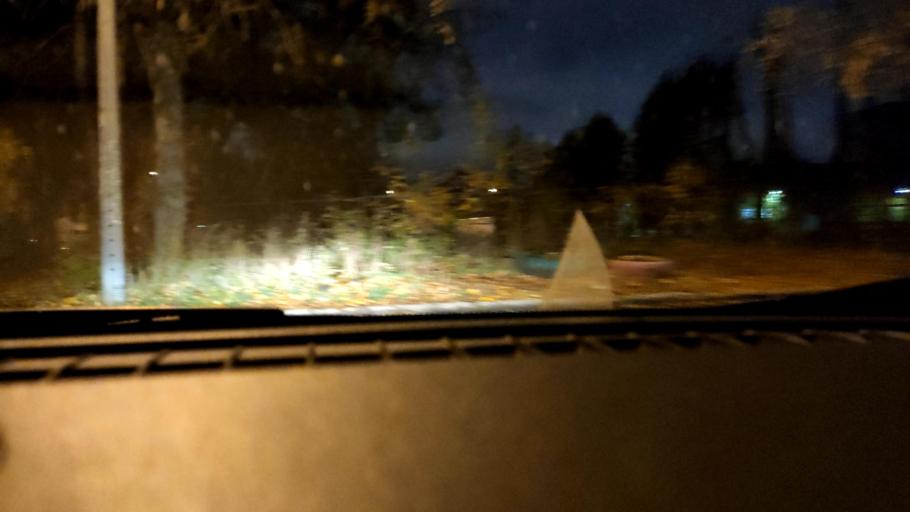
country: RU
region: Perm
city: Perm
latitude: 57.9620
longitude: 56.2221
